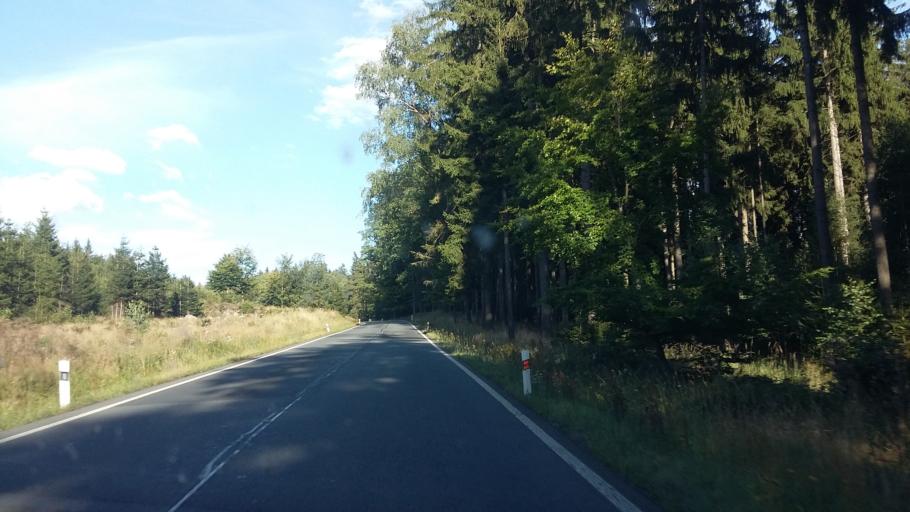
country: CZ
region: Plzensky
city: Mirosov
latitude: 49.6219
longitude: 13.7371
